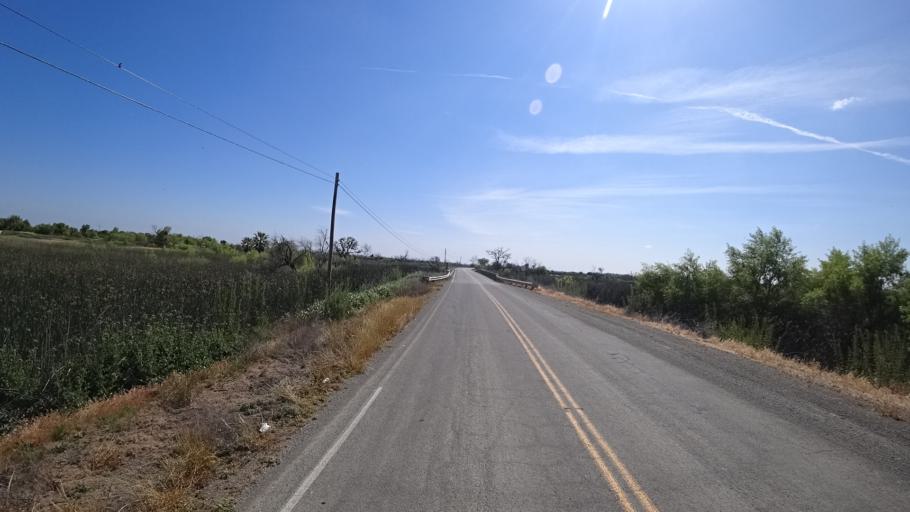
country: US
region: California
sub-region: Kings County
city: Lemoore Station
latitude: 36.2556
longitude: -119.8602
